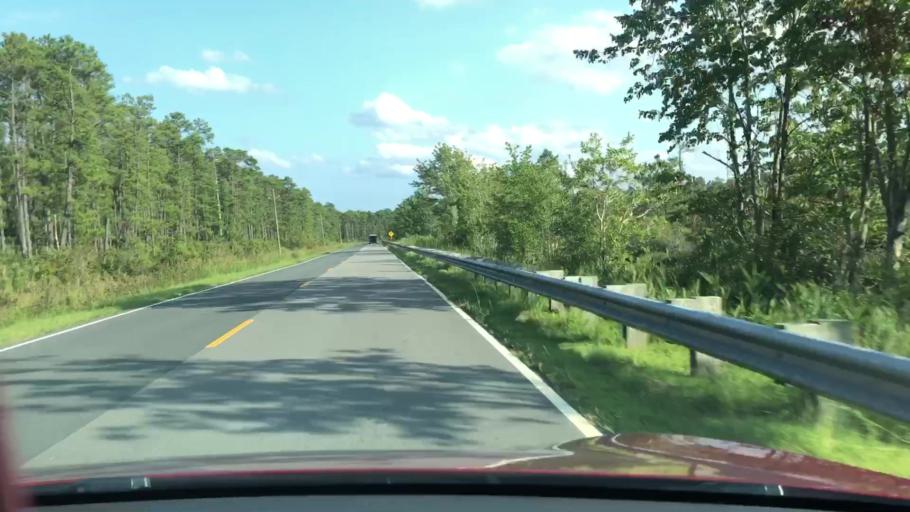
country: US
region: North Carolina
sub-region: Dare County
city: Wanchese
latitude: 35.7906
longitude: -75.7725
